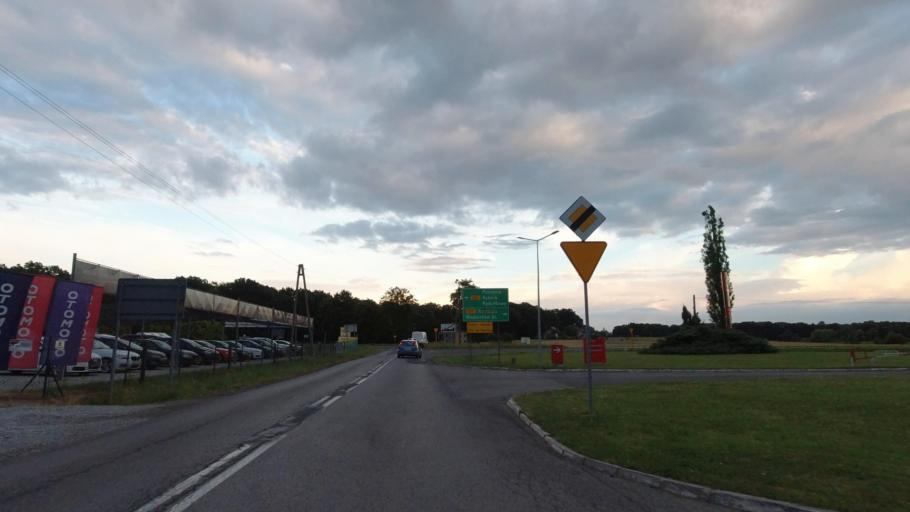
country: PL
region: Silesian Voivodeship
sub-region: Powiat rybnicki
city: Czernica
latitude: 50.0735
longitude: 18.3730
